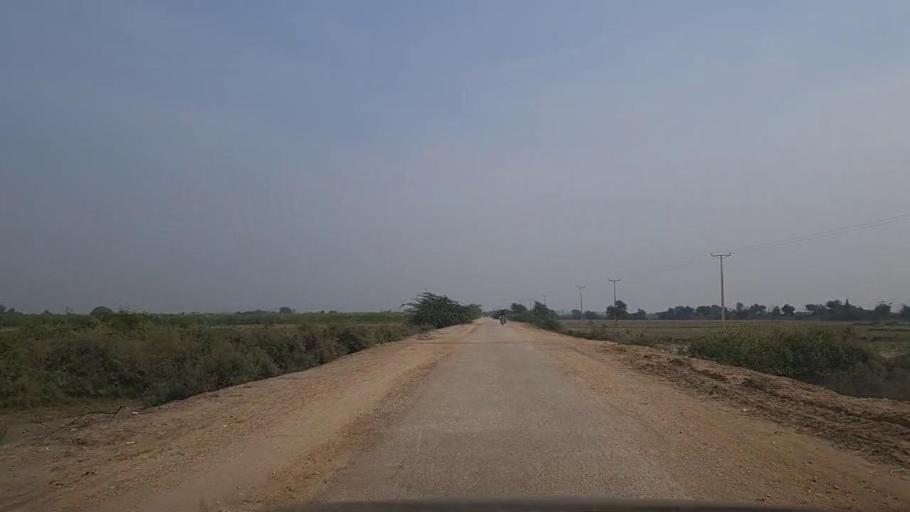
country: PK
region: Sindh
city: Mirpur Sakro
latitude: 24.4026
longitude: 67.7441
